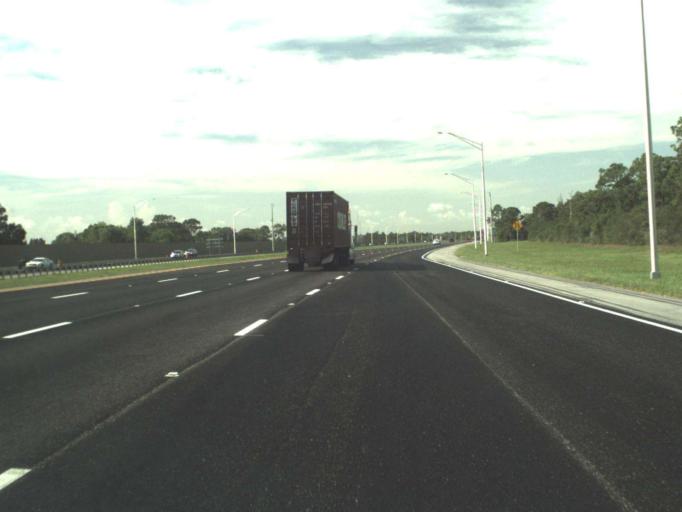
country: US
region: Florida
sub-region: Indian River County
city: West Vero Corridor
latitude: 27.6326
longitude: -80.5160
